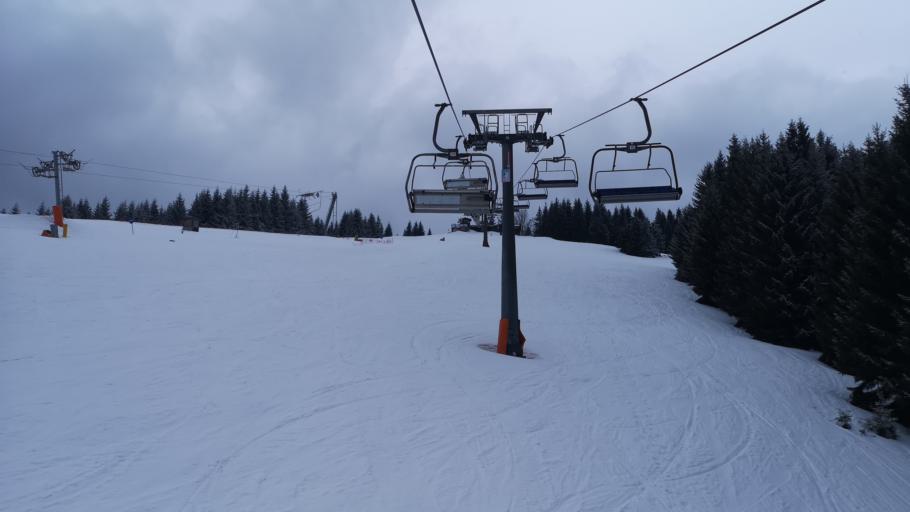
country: SK
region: Zilinsky
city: Ruzomberok
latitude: 49.0502
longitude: 19.2524
